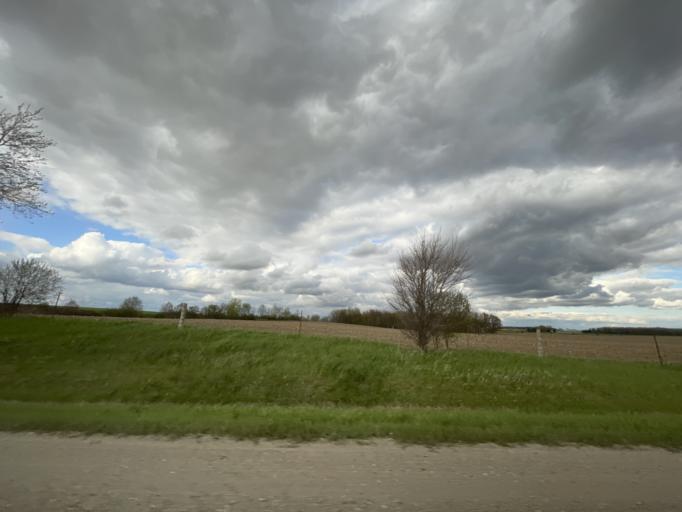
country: CA
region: Ontario
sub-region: Wellington County
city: Guelph
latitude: 43.5143
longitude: -80.3174
